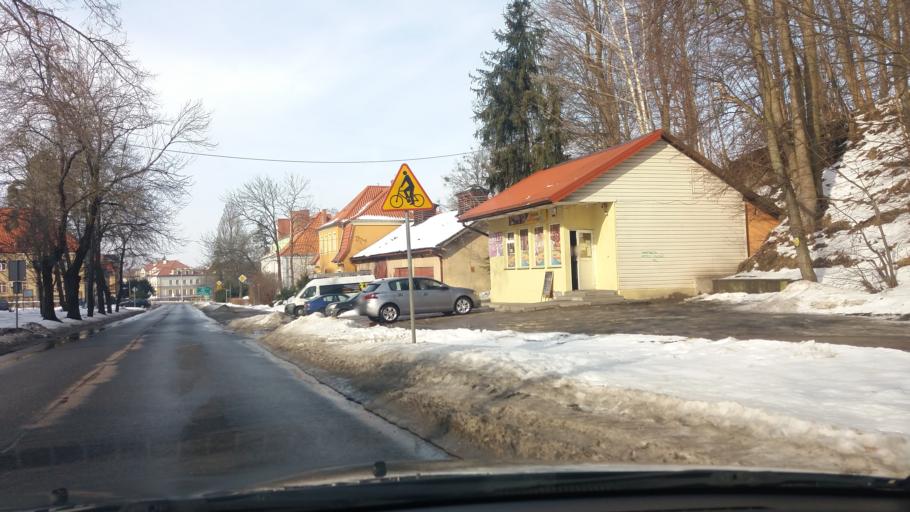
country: PL
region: Warmian-Masurian Voivodeship
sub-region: Powiat lidzbarski
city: Lidzbark Warminski
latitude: 54.1236
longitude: 20.5924
